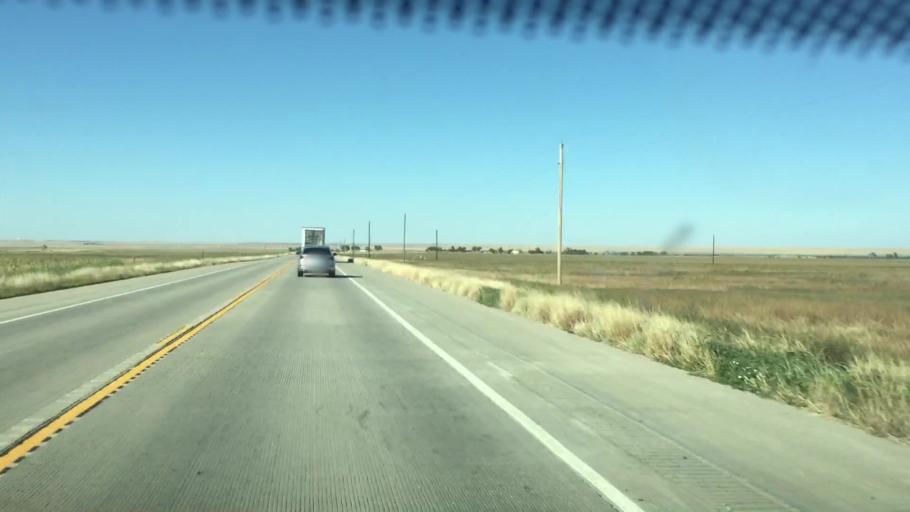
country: US
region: Colorado
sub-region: Kiowa County
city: Eads
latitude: 38.3155
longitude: -102.7199
